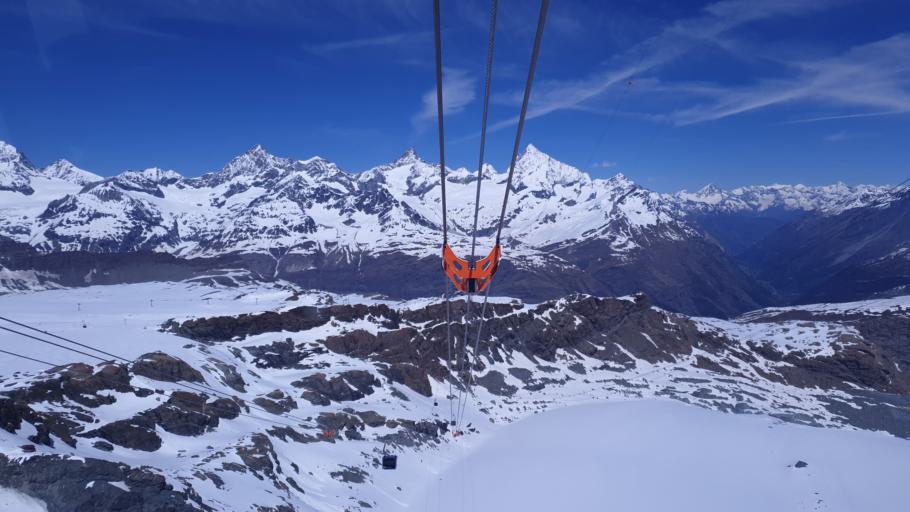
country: CH
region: Valais
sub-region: Visp District
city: Zermatt
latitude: 45.9471
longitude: 7.7273
